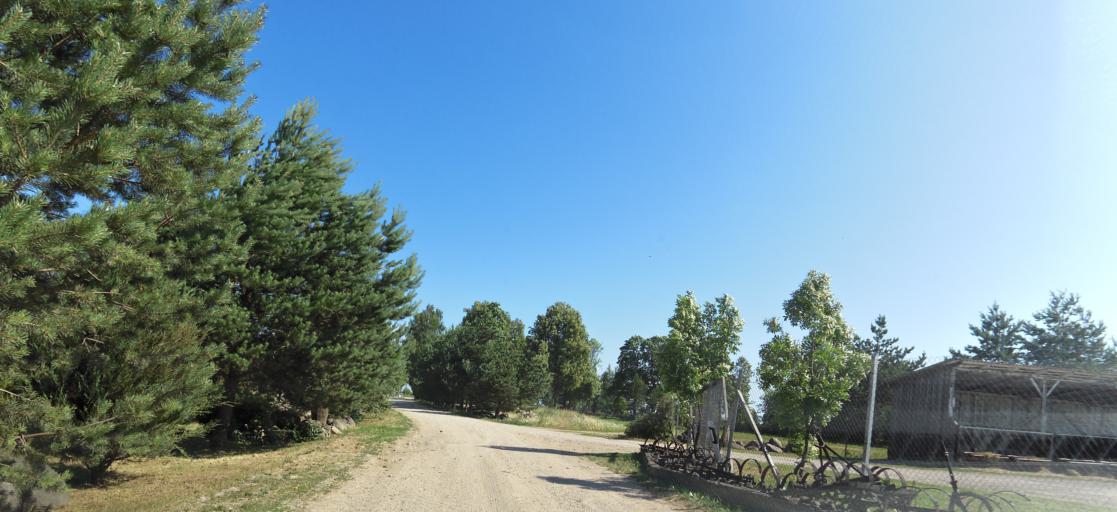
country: LT
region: Panevezys
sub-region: Birzai
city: Birzai
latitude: 56.2443
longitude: 24.8772
